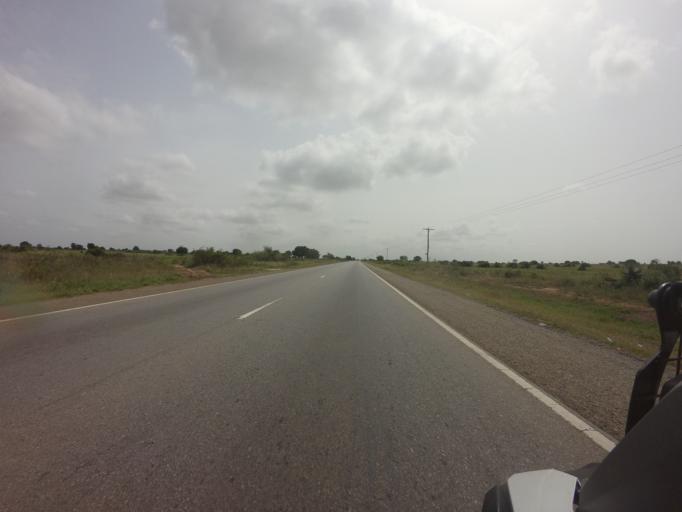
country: GH
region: Volta
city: Anloga
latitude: 5.8849
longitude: 0.4363
